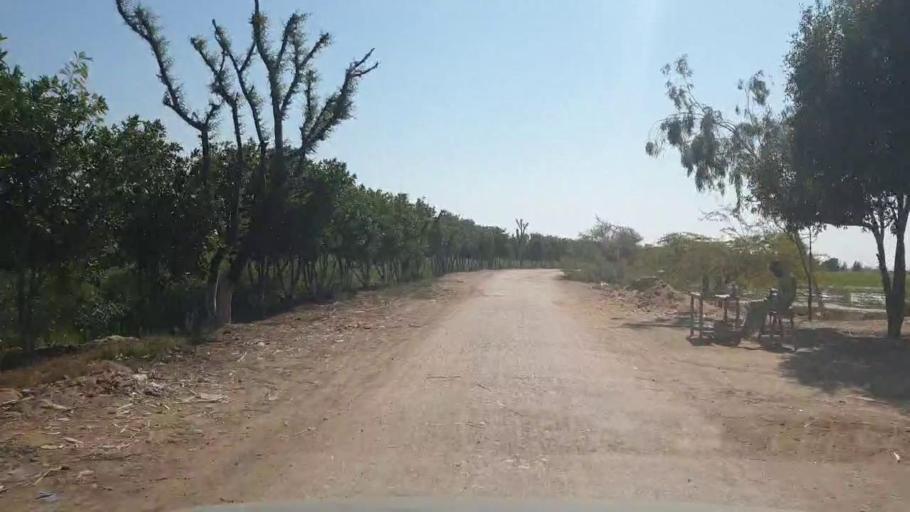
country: PK
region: Sindh
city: Mirwah Gorchani
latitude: 25.3096
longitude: 69.1290
